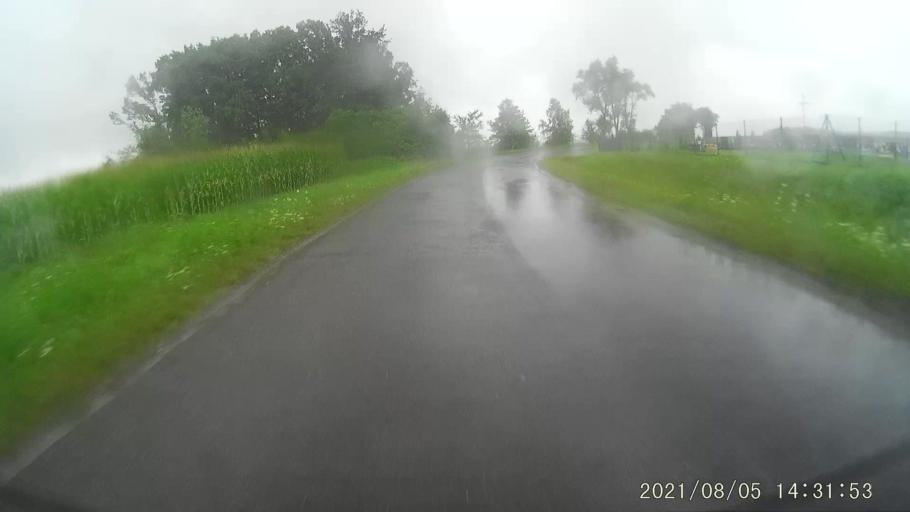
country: PL
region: Opole Voivodeship
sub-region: Powiat nyski
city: Korfantow
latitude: 50.4710
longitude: 17.5529
